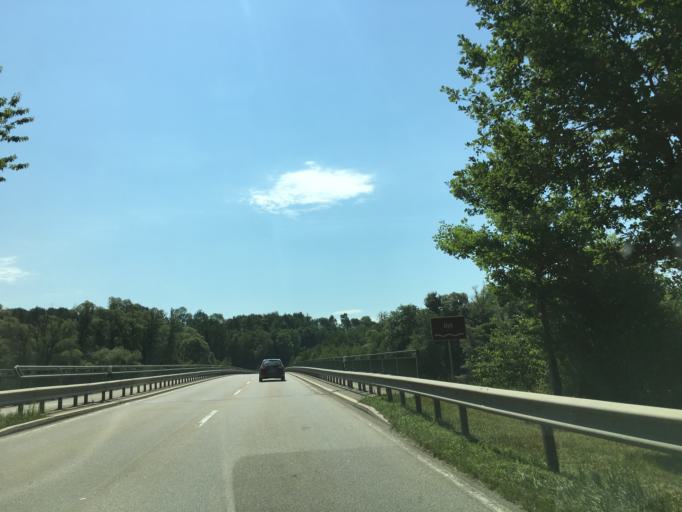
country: DE
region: Bavaria
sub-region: Upper Bavaria
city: Griesstatt
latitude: 47.9956
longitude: 12.1632
